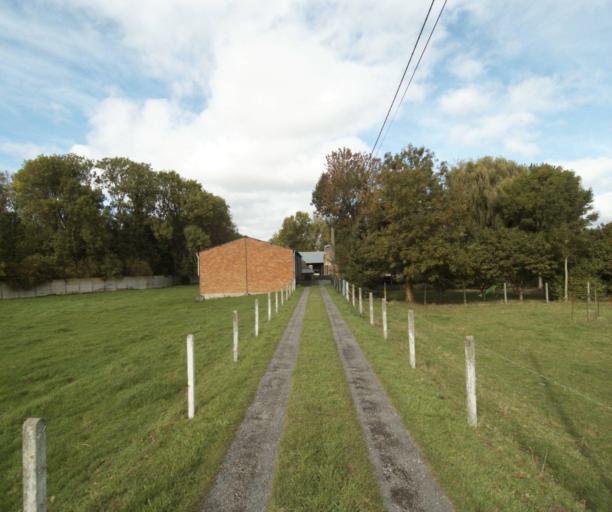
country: FR
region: Nord-Pas-de-Calais
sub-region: Departement du Nord
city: Houplines
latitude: 50.6913
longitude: 2.9063
